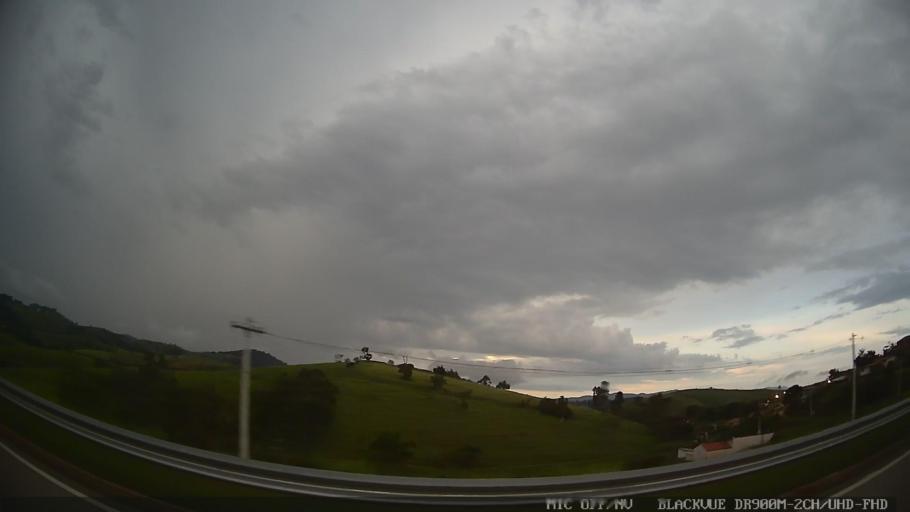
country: BR
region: Sao Paulo
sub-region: Santa Branca
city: Santa Branca
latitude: -23.4252
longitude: -45.6326
